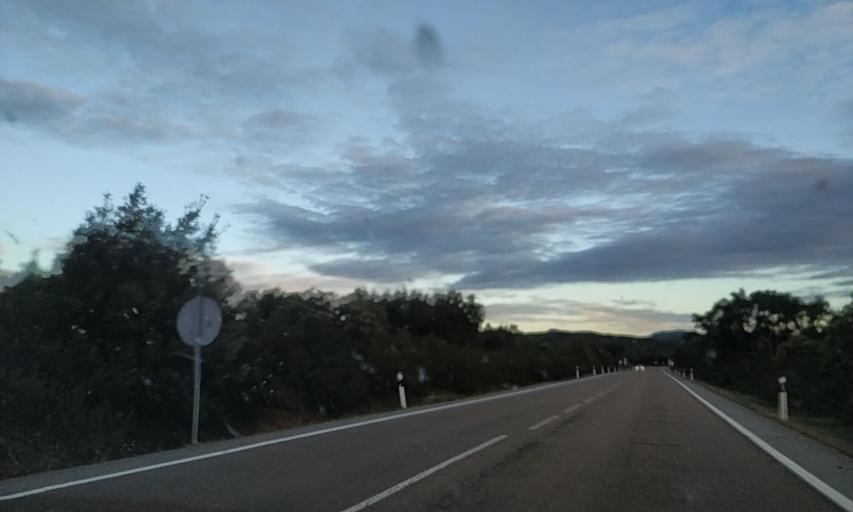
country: ES
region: Extremadura
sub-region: Provincia de Badajoz
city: Puebla de Obando
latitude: 39.2800
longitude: -6.5212
